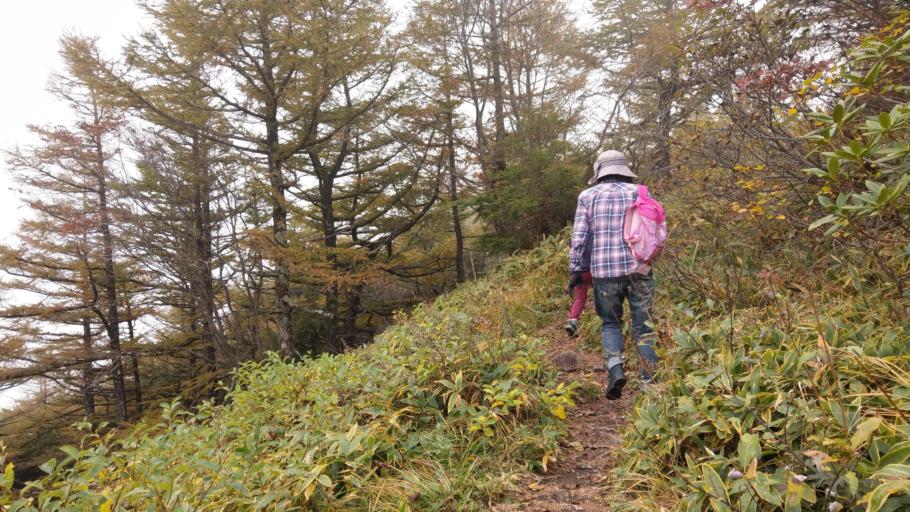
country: JP
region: Nagano
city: Komoro
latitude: 36.4039
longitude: 138.4591
